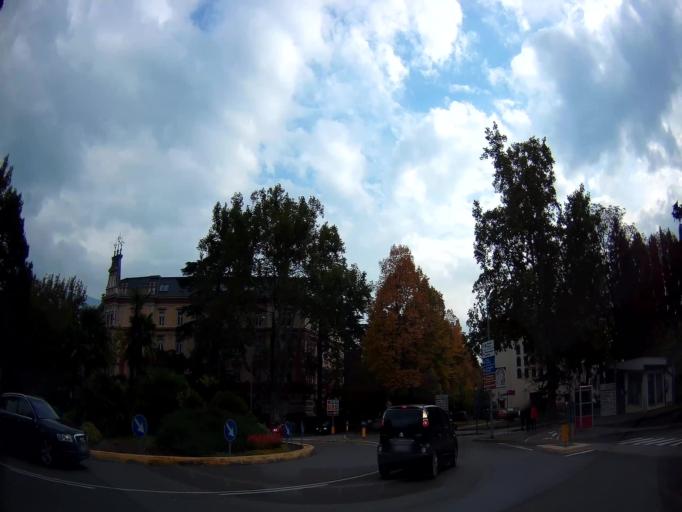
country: IT
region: Trentino-Alto Adige
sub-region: Bolzano
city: Merano
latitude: 46.6713
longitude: 11.1521
